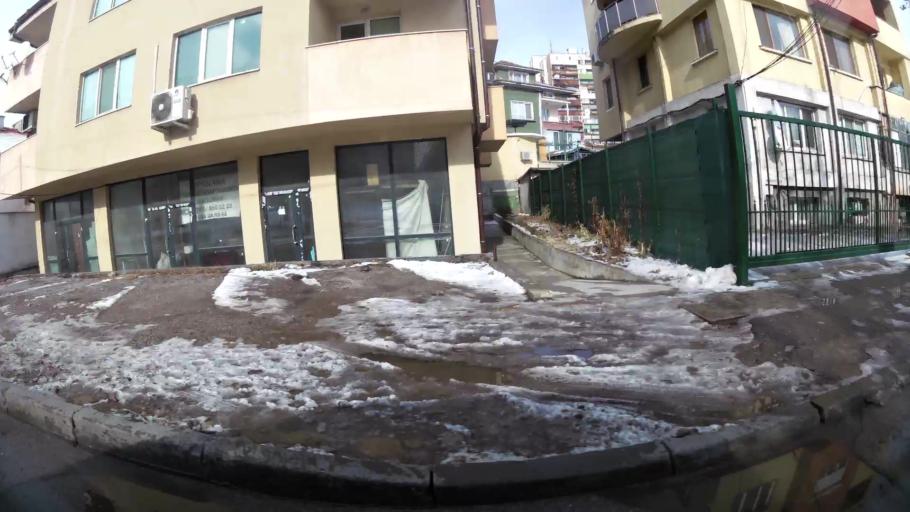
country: BG
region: Sofia-Capital
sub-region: Stolichna Obshtina
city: Sofia
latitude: 42.7074
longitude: 23.3570
